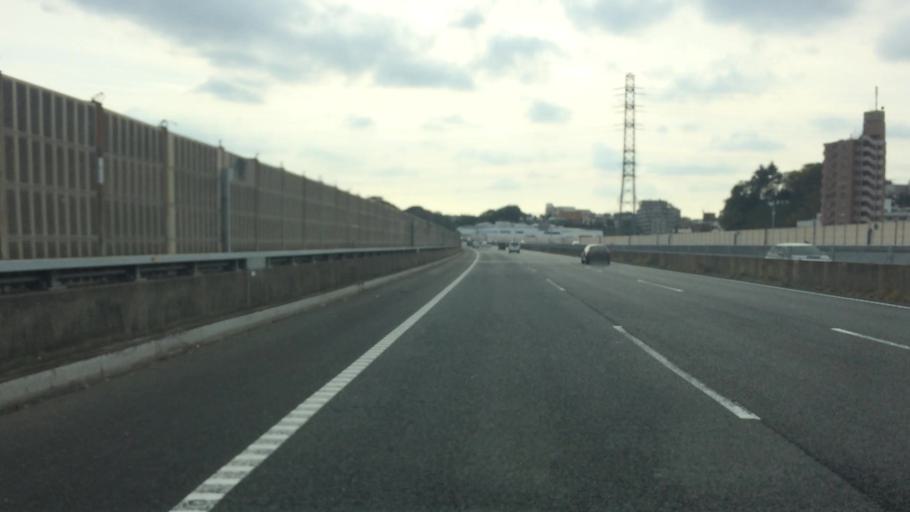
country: JP
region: Tokyo
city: Chofugaoka
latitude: 35.5878
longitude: 139.6216
